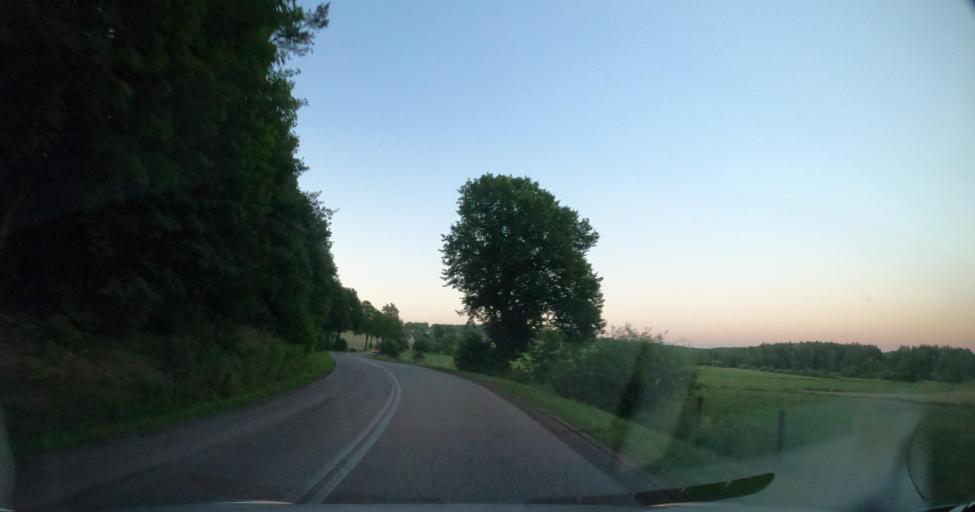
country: PL
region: Pomeranian Voivodeship
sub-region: Powiat wejherowski
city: Luzino
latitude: 54.4648
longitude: 18.0621
